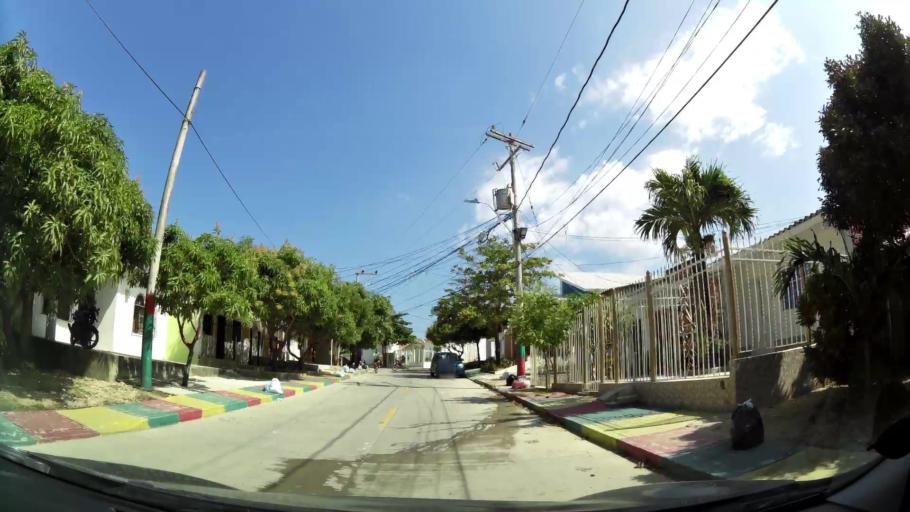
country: CO
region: Atlantico
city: Barranquilla
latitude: 10.9674
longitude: -74.8321
